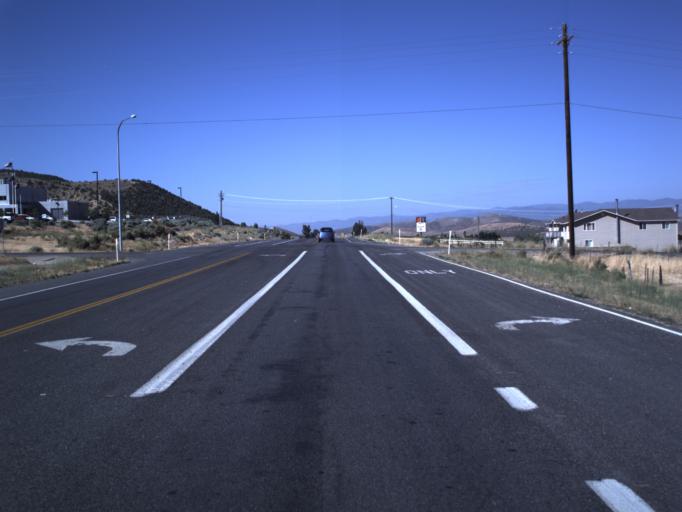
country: US
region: Utah
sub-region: Sanpete County
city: Manti
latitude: 39.2500
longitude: -111.6442
